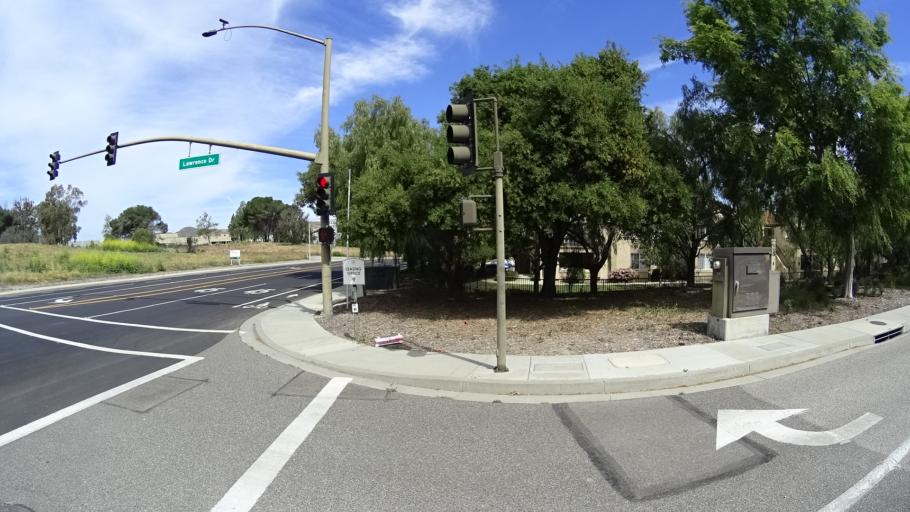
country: US
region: California
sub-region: Ventura County
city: Casa Conejo
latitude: 34.2000
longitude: -118.9237
